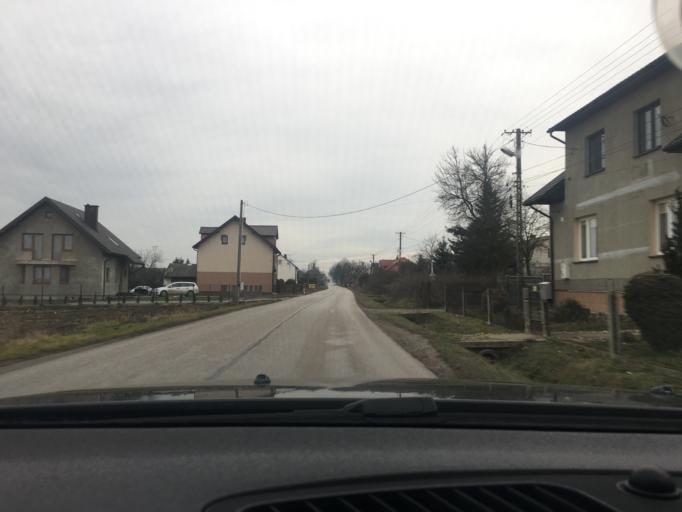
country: PL
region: Swietokrzyskie
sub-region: Powiat jedrzejowski
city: Jedrzejow
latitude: 50.6407
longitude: 20.3603
